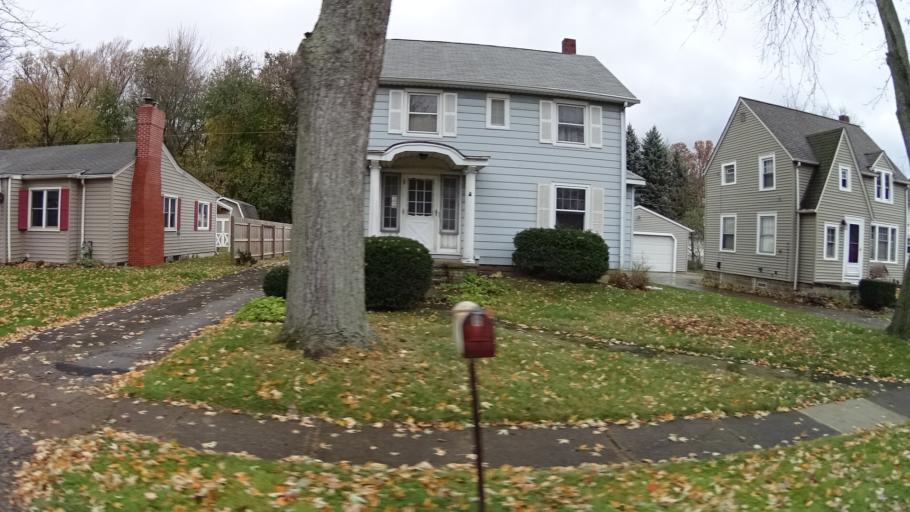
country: US
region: Ohio
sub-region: Lorain County
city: Elyria
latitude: 41.3897
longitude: -82.1310
